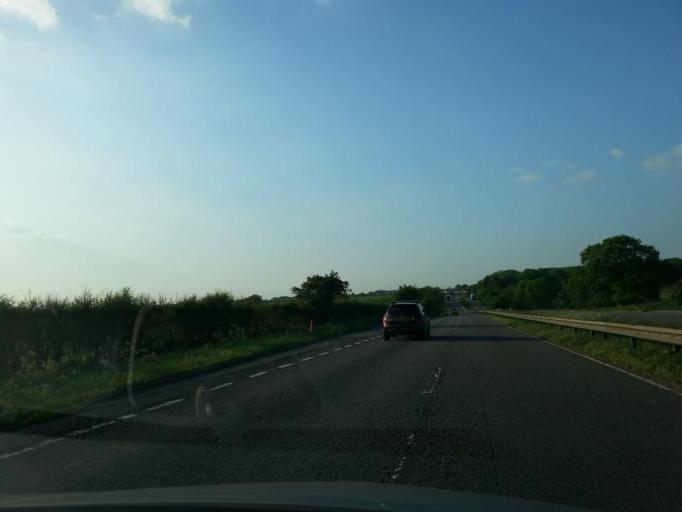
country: GB
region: England
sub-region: District of Rutland
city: Clipsham
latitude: 52.7894
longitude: -0.6108
